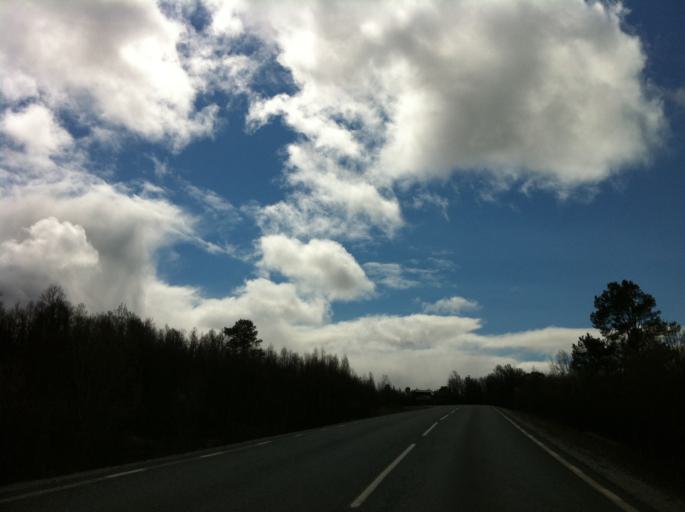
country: NO
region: Sor-Trondelag
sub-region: Tydal
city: Aas
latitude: 62.6455
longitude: 12.4280
